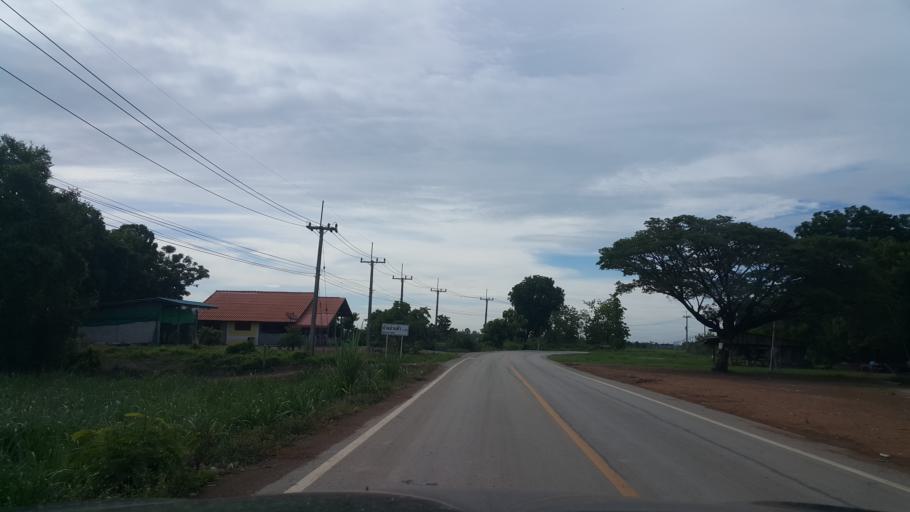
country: TH
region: Sukhothai
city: Si Nakhon
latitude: 17.2788
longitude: 99.9744
